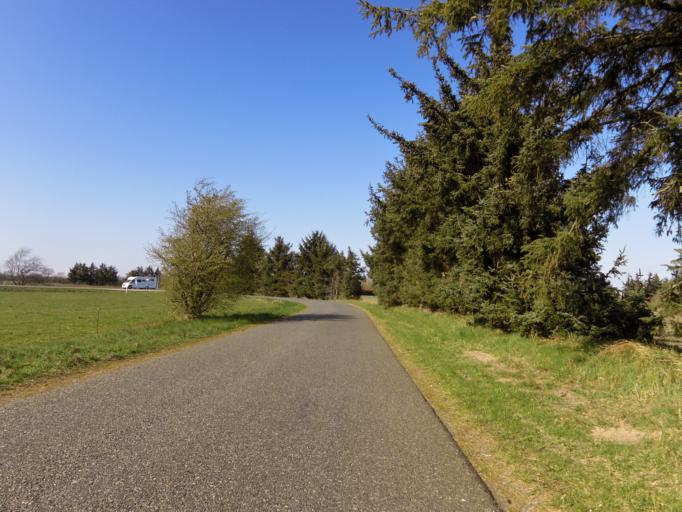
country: DK
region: South Denmark
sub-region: Esbjerg Kommune
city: Ribe
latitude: 55.3671
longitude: 8.8073
